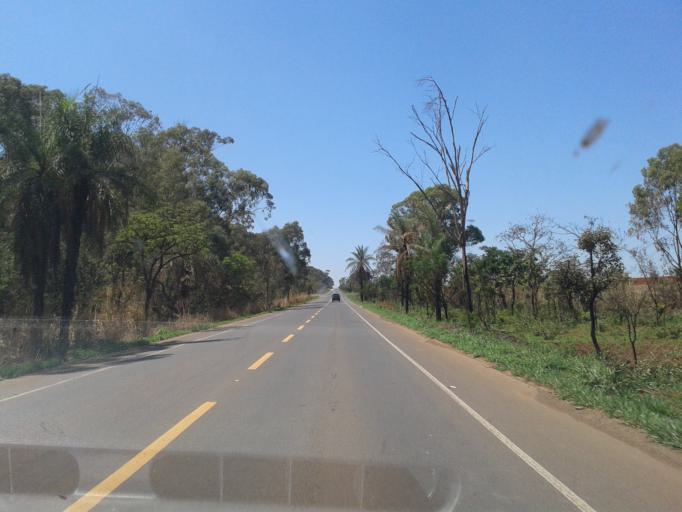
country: BR
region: Minas Gerais
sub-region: Araxa
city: Araxa
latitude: -19.3919
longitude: -47.3337
